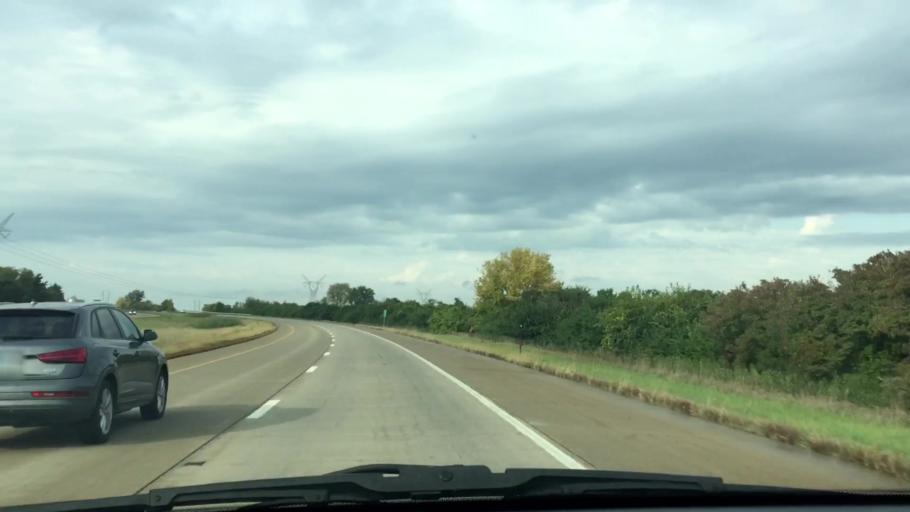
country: US
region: Illinois
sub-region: Whiteside County
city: Morrison
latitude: 41.7653
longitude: -89.8425
